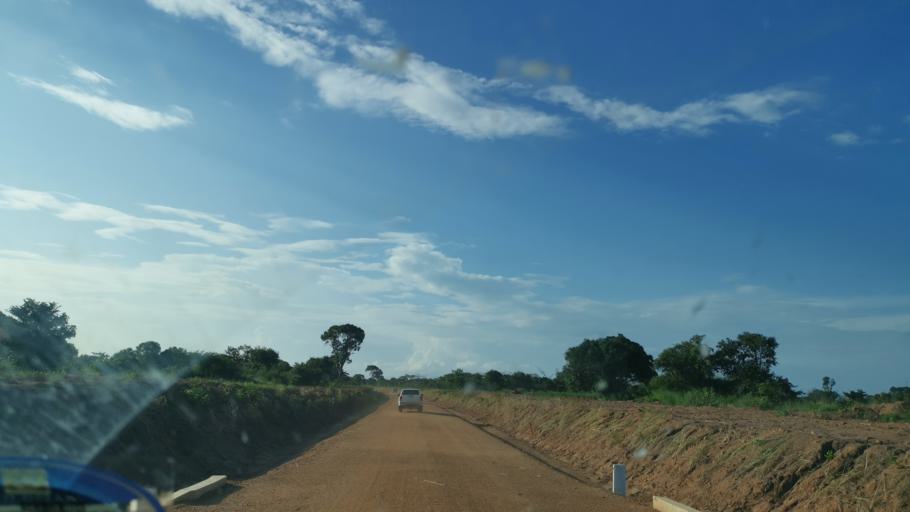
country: ZM
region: Luapula
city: Samfya
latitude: -11.1072
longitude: 29.5745
